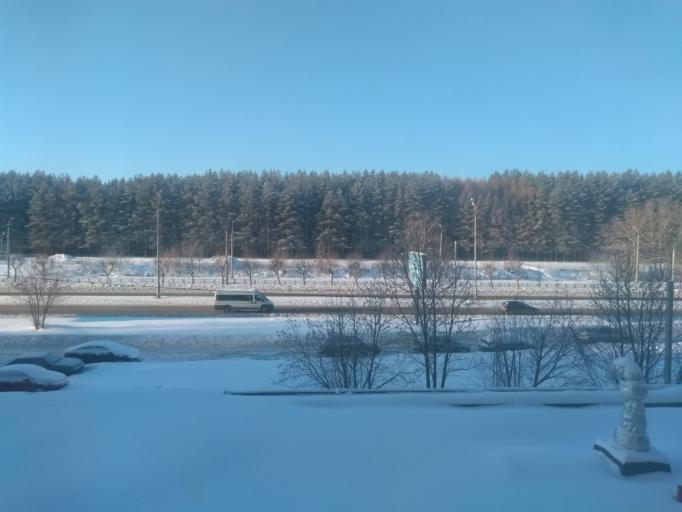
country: RU
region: Udmurtiya
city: Khokhryaki
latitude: 56.8642
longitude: 53.2786
